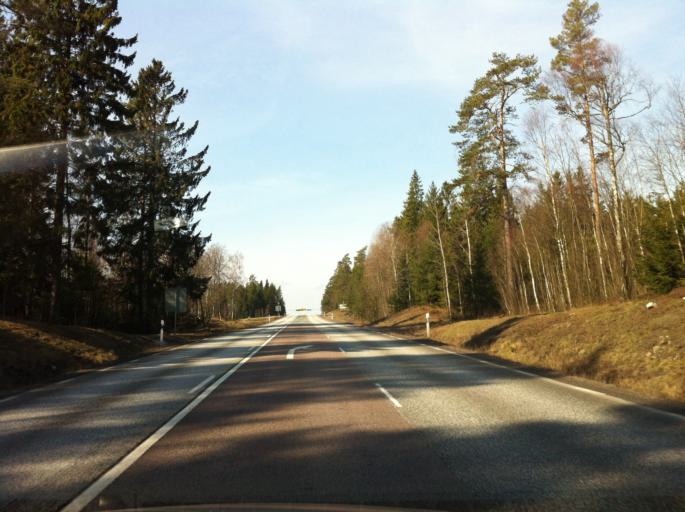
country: SE
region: Joenkoeping
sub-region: Mullsjo Kommun
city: Mullsjoe
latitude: 57.8714
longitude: 13.9442
